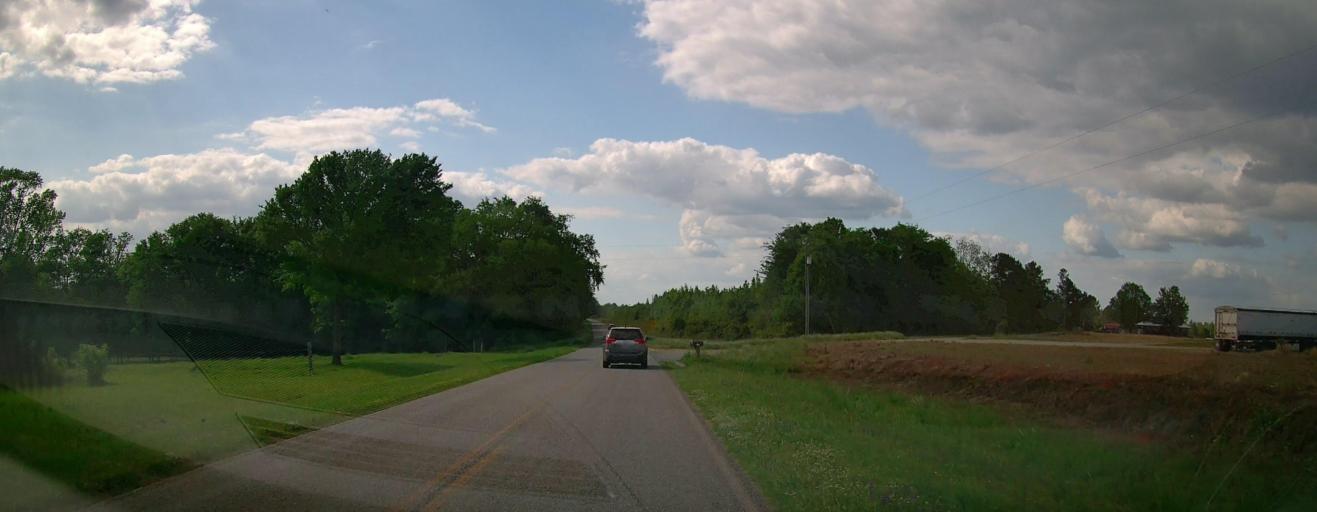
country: US
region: Georgia
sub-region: Laurens County
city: East Dublin
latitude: 32.6873
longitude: -82.8960
